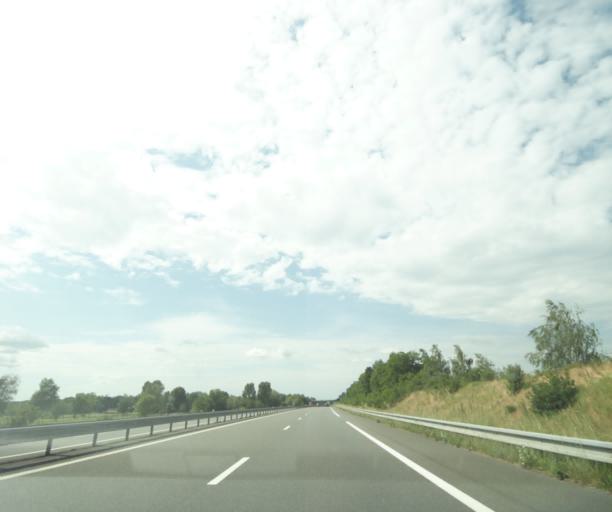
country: FR
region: Pays de la Loire
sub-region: Departement de Maine-et-Loire
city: Jumelles
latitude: 47.3933
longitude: -0.1093
